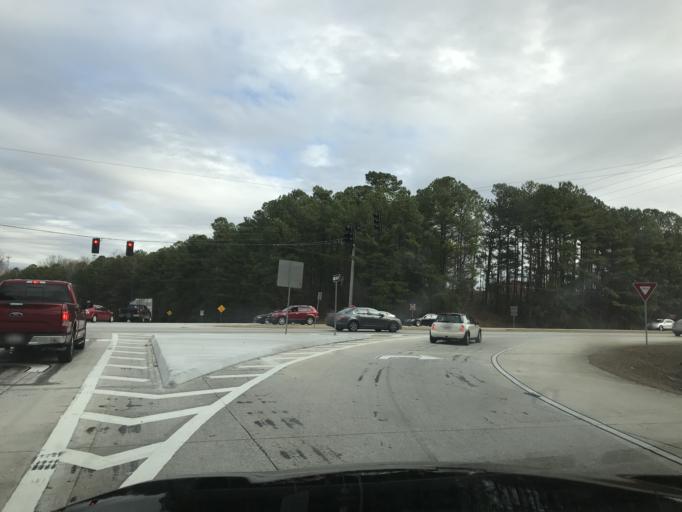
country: US
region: Georgia
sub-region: Carroll County
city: Villa Rica
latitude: 33.7208
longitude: -84.9395
